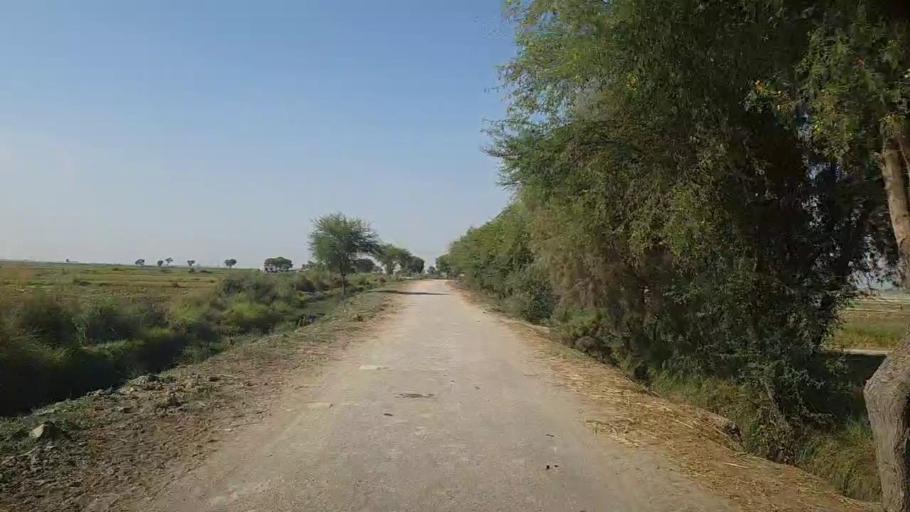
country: PK
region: Sindh
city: Tangwani
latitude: 28.2484
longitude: 68.9441
